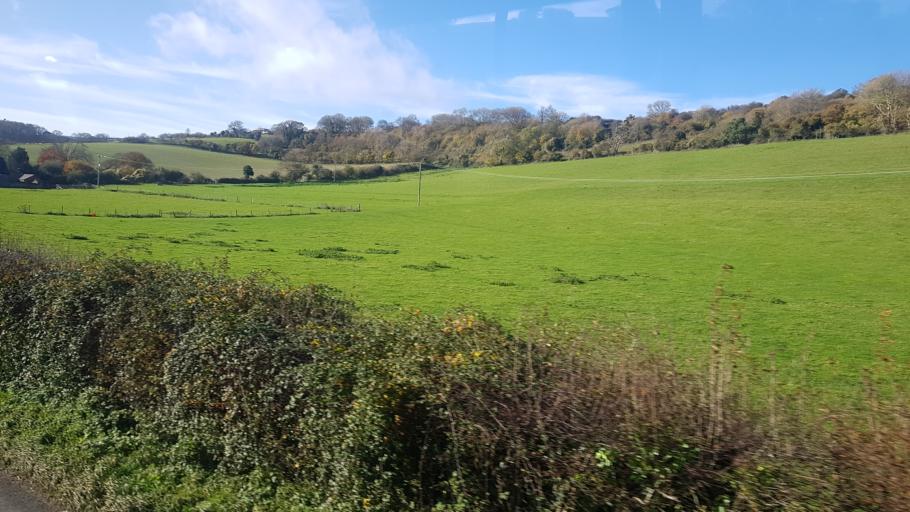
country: GB
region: England
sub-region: Isle of Wight
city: Newport
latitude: 50.6752
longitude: -1.3419
